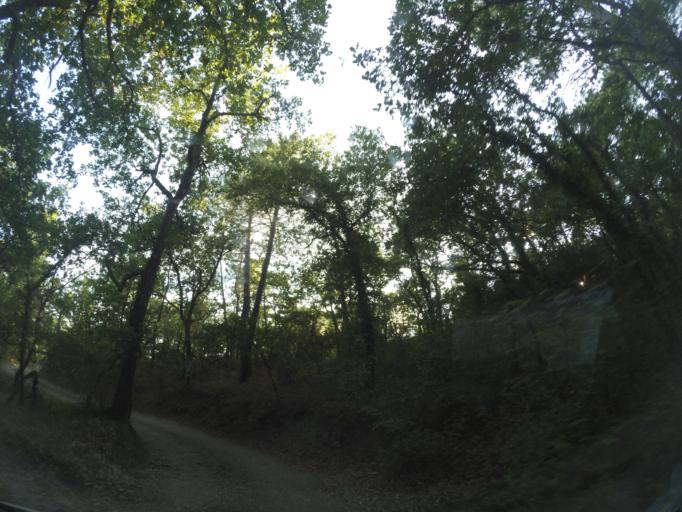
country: IT
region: Tuscany
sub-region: Province of Arezzo
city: Castiglion Fibocchi
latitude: 43.5491
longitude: 11.7880
